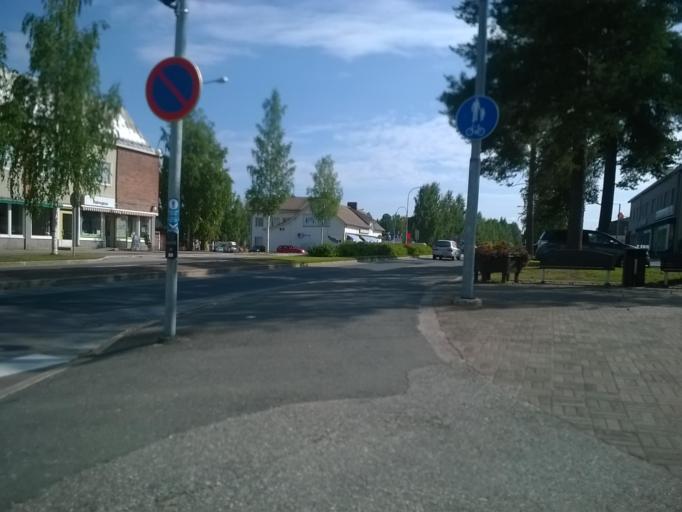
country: FI
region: Kainuu
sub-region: Kehys-Kainuu
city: Kuhmo
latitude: 64.1280
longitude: 29.5218
